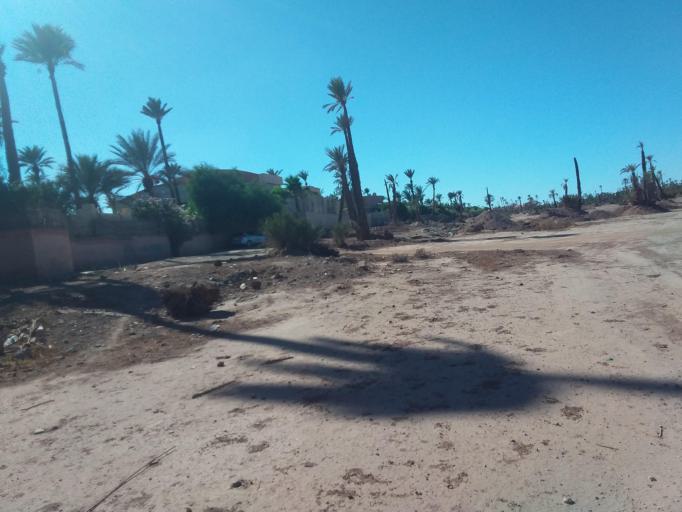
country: MA
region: Marrakech-Tensift-Al Haouz
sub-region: Marrakech
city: Marrakesh
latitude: 31.6801
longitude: -7.9534
